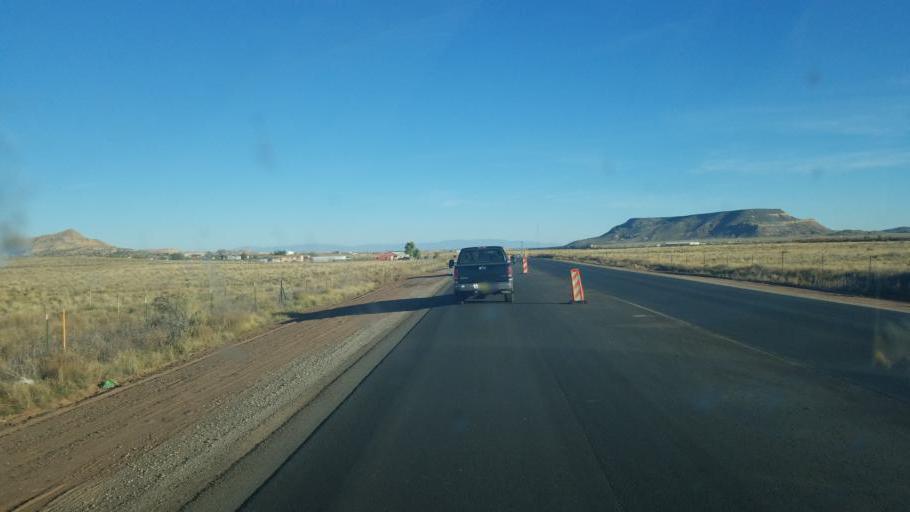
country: US
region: New Mexico
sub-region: Cibola County
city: Laguna
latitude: 34.9520
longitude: -107.1702
